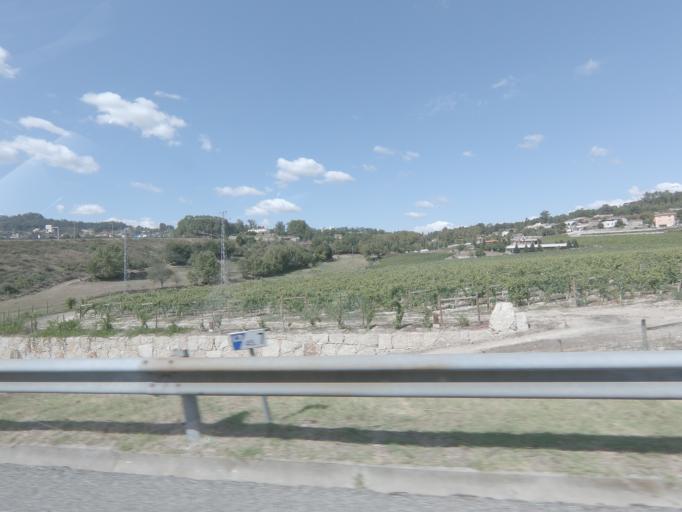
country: PT
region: Porto
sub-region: Lousada
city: Meinedo
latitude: 41.2352
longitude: -8.1975
